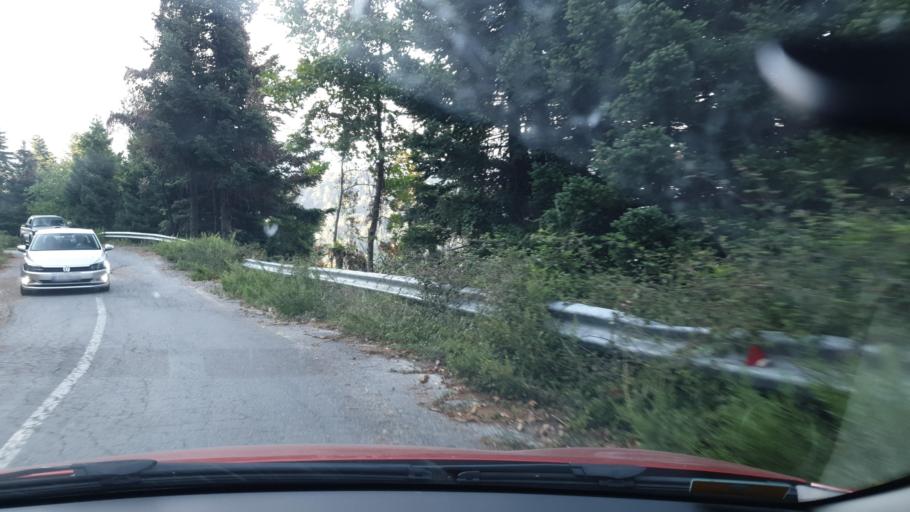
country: GR
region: Central Greece
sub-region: Nomos Evvoias
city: Yimnon
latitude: 38.5985
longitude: 23.9020
